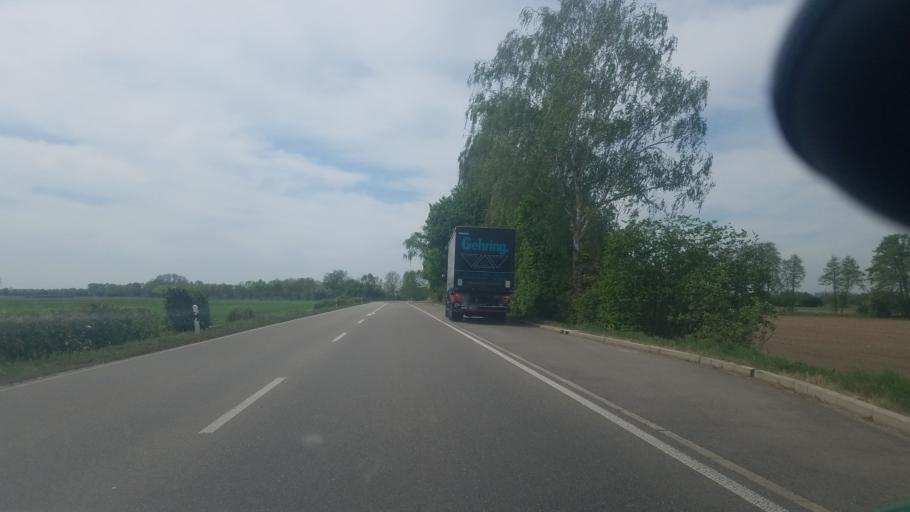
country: DE
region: Baden-Wuerttemberg
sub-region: Freiburg Region
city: Kehl
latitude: 48.5896
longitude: 7.8429
